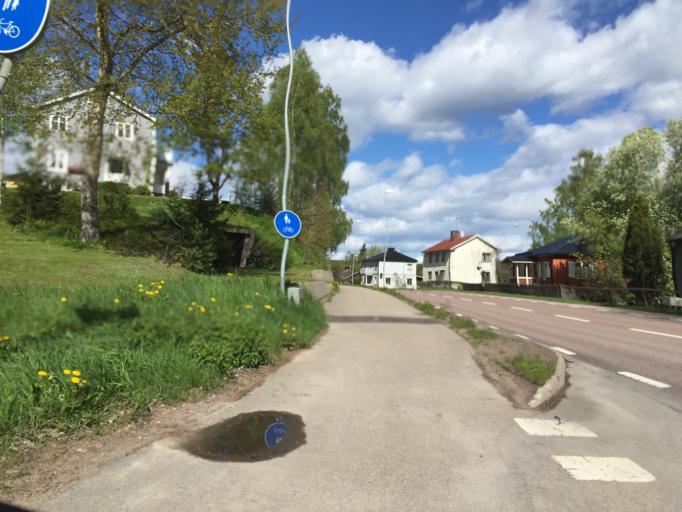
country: SE
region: Dalarna
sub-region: Ludvika Kommun
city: Ludvika
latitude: 60.1587
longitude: 15.1915
